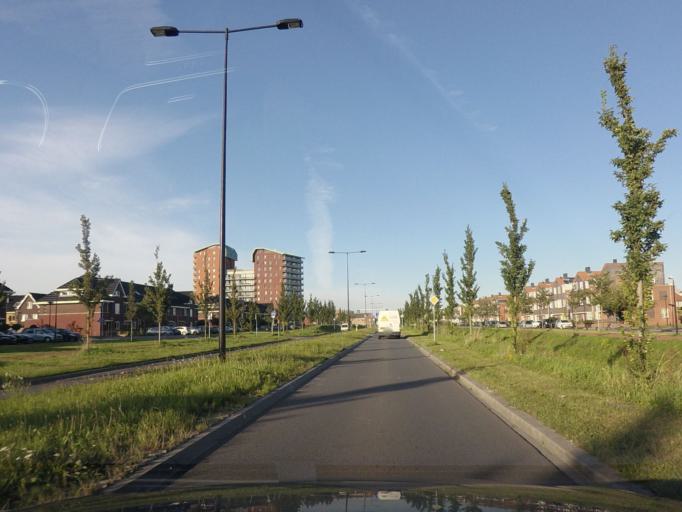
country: NL
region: North Holland
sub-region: Gemeente Beverwijk
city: Beverwijk
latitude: 52.4858
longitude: 4.6783
